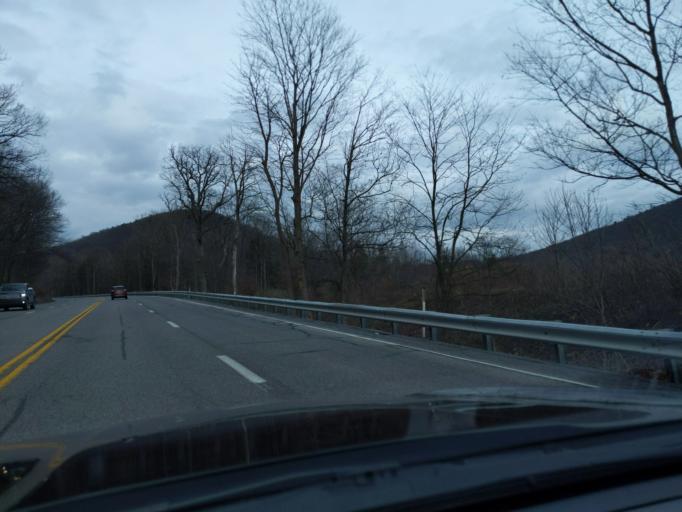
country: US
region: Pennsylvania
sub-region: Blair County
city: Williamsburg
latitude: 40.4893
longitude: -78.2455
